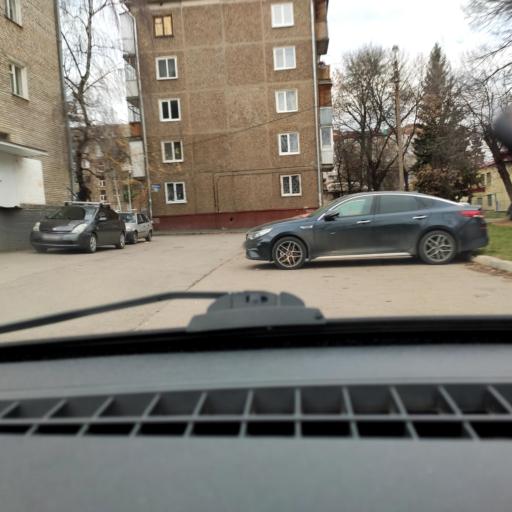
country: RU
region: Bashkortostan
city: Ufa
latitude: 54.8179
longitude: 56.1133
